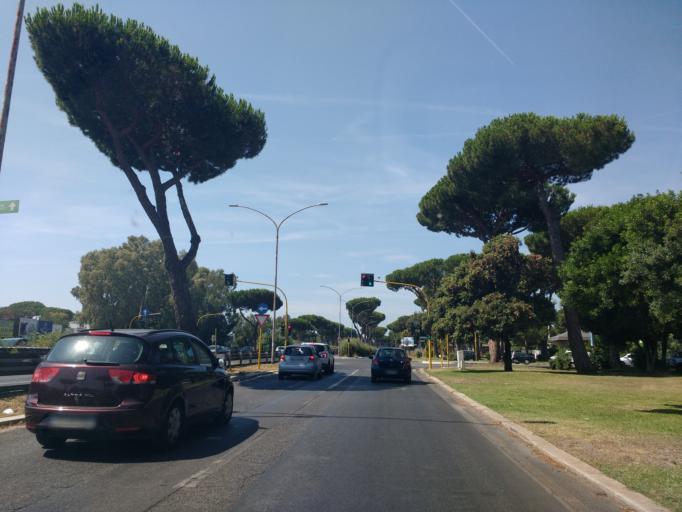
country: IT
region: Latium
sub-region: Citta metropolitana di Roma Capitale
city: Acilia-Castel Fusano-Ostia Antica
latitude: 41.7462
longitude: 12.3581
